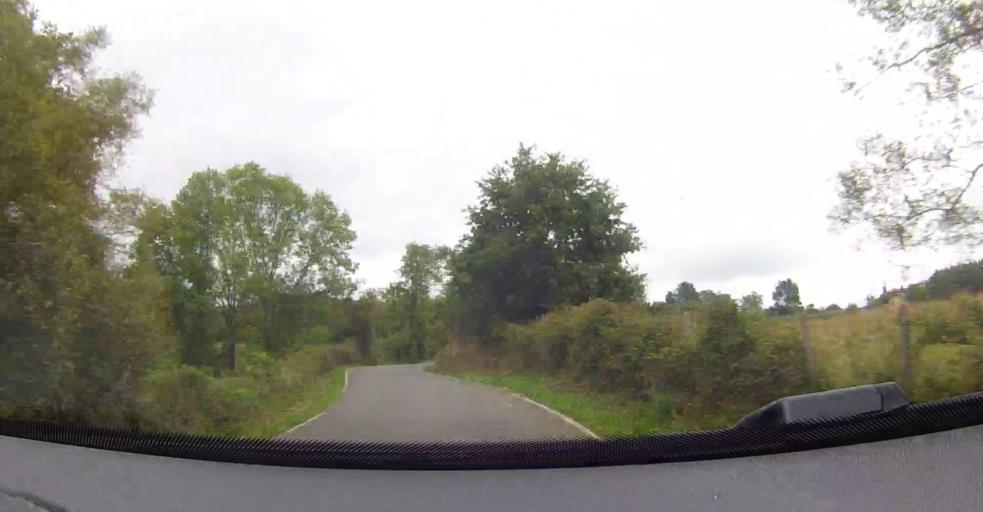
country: ES
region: Basque Country
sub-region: Bizkaia
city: Urrestieta
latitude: 43.2326
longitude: -3.1884
